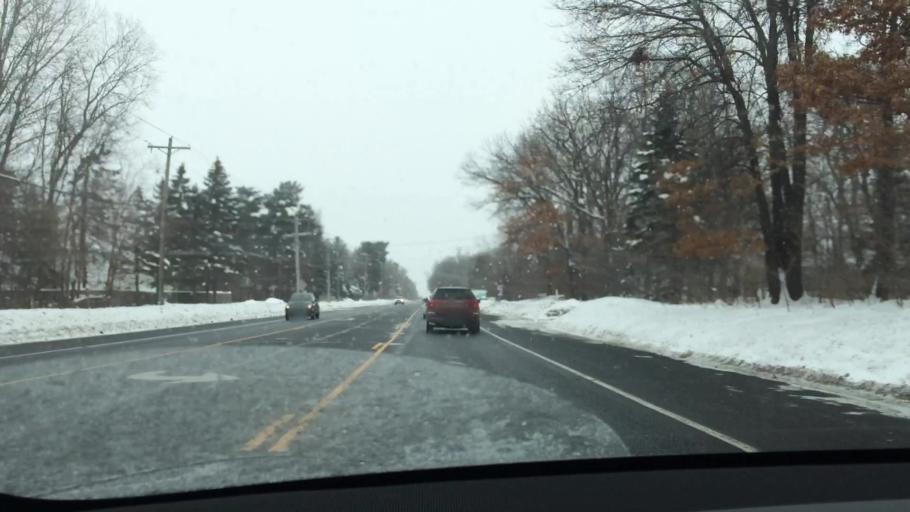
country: US
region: Minnesota
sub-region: Ramsey County
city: Shoreview
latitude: 45.0928
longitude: -93.1271
